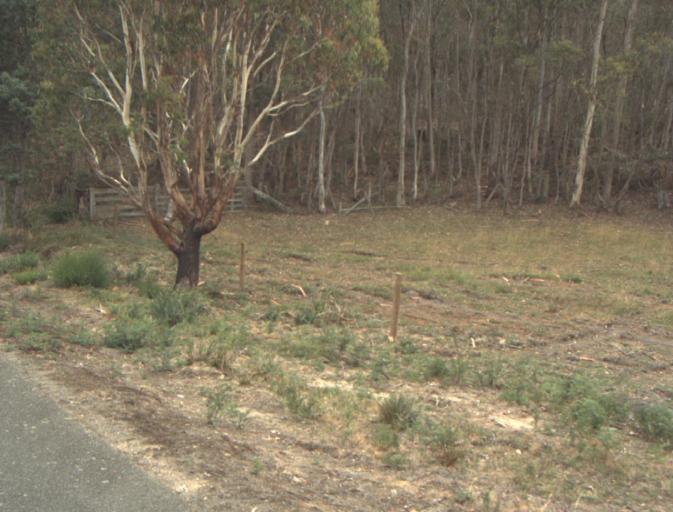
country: AU
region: Tasmania
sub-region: Northern Midlands
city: Evandale
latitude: -41.4696
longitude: 147.4957
